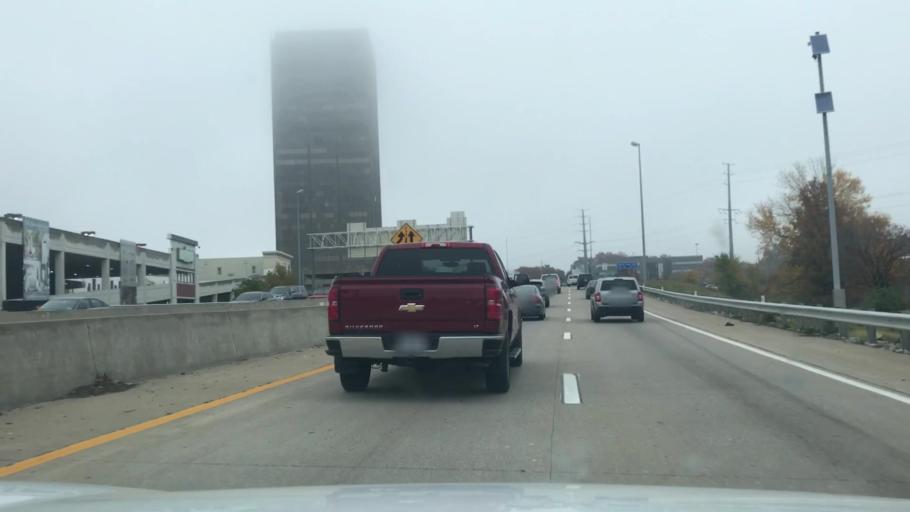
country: US
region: Missouri
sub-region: Saint Louis County
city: Brentwood
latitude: 38.6336
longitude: -90.3440
